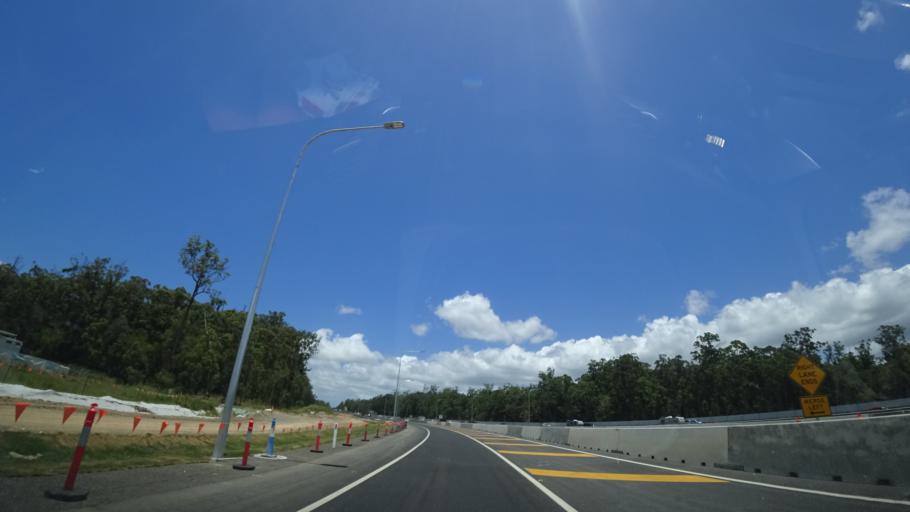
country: AU
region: Queensland
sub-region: Sunshine Coast
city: Little Mountain
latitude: -26.7769
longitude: 153.0439
